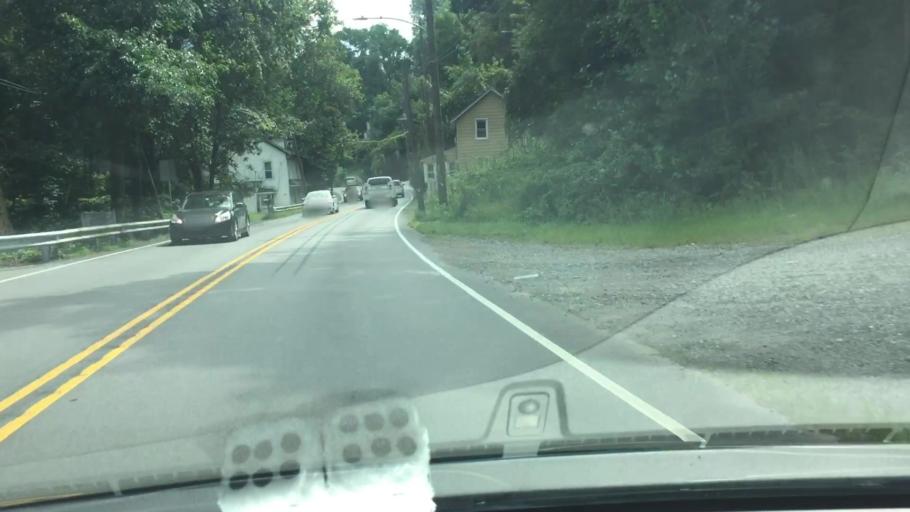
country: US
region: Pennsylvania
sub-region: Delaware County
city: Village Green-Green Ridge
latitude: 39.8873
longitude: -75.4310
